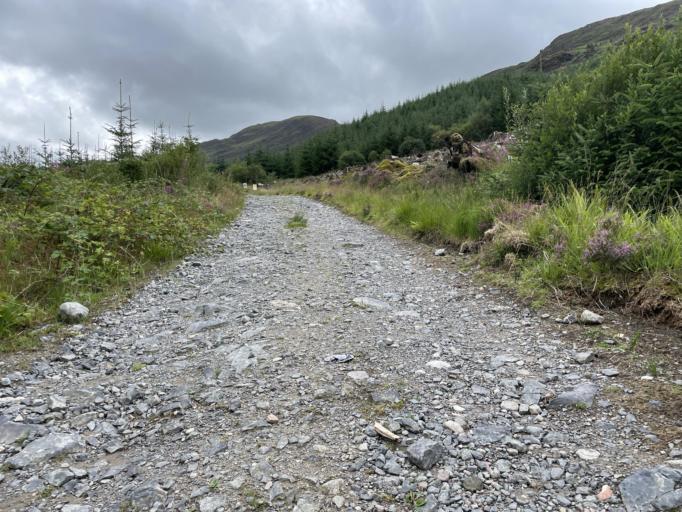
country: GB
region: Scotland
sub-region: Dumfries and Galloway
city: Newton Stewart
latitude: 55.0865
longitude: -4.4569
